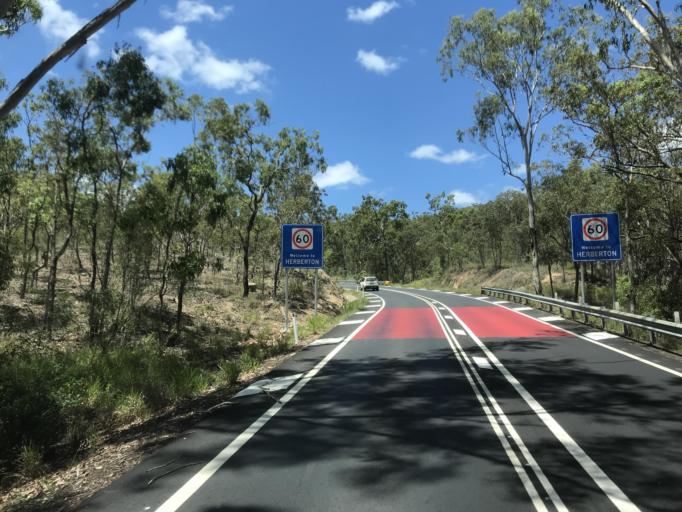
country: AU
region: Queensland
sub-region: Tablelands
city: Atherton
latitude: -17.3999
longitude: 145.3900
